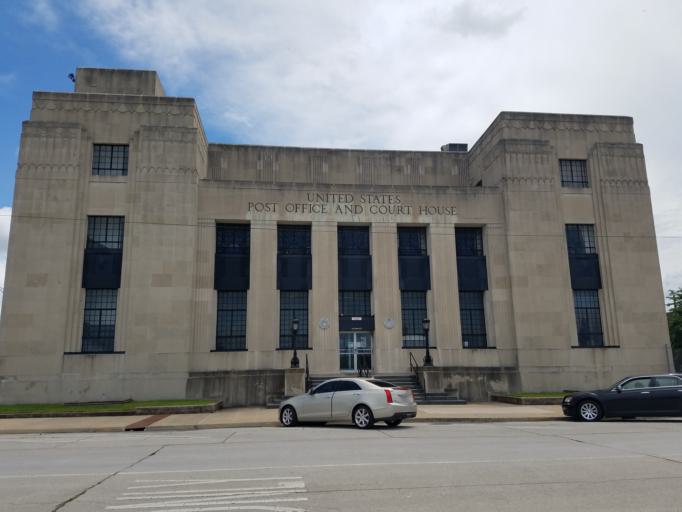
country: US
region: Oklahoma
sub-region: Pontotoc County
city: Ada
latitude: 34.7735
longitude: -96.6768
